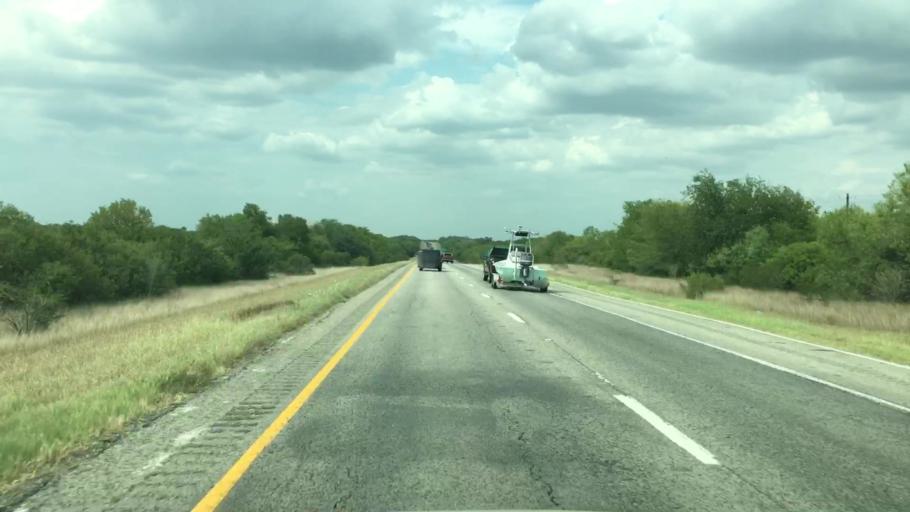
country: US
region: Texas
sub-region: Atascosa County
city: Pleasanton
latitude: 28.9261
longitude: -98.4349
